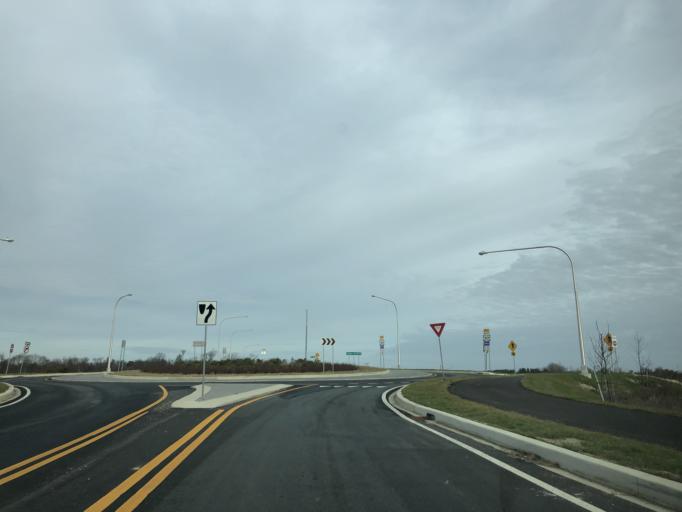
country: US
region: Delaware
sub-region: New Castle County
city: Middletown
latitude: 39.5227
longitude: -75.6795
